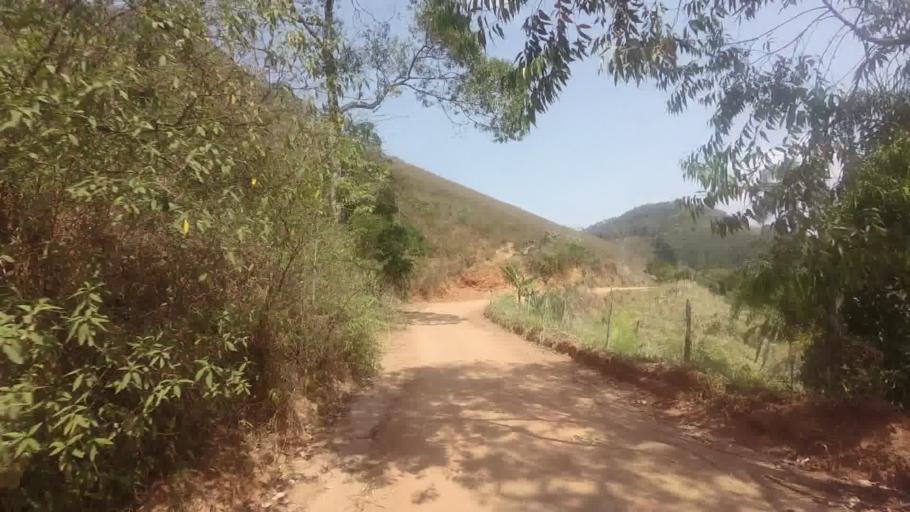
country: BR
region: Espirito Santo
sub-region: Mimoso Do Sul
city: Mimoso do Sul
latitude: -20.9943
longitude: -41.5019
